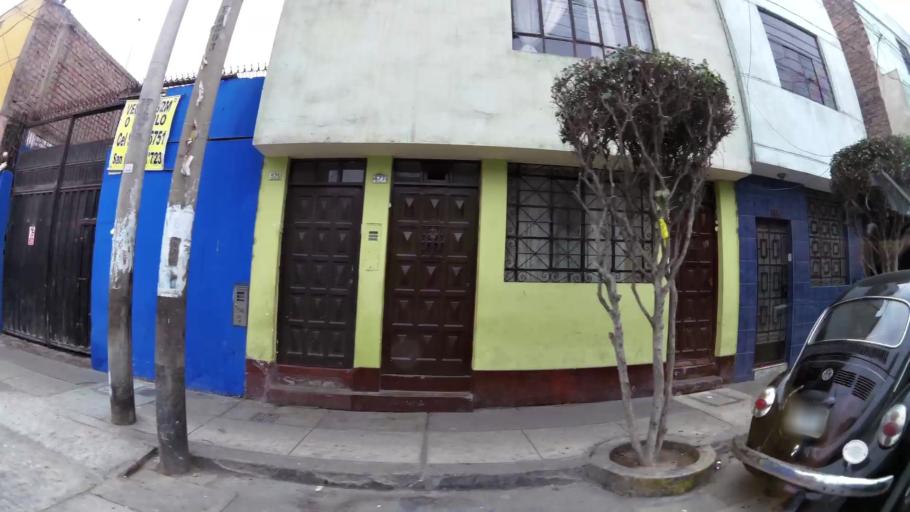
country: PE
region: Lima
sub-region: Lima
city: Surco
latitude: -12.1142
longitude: -77.0203
